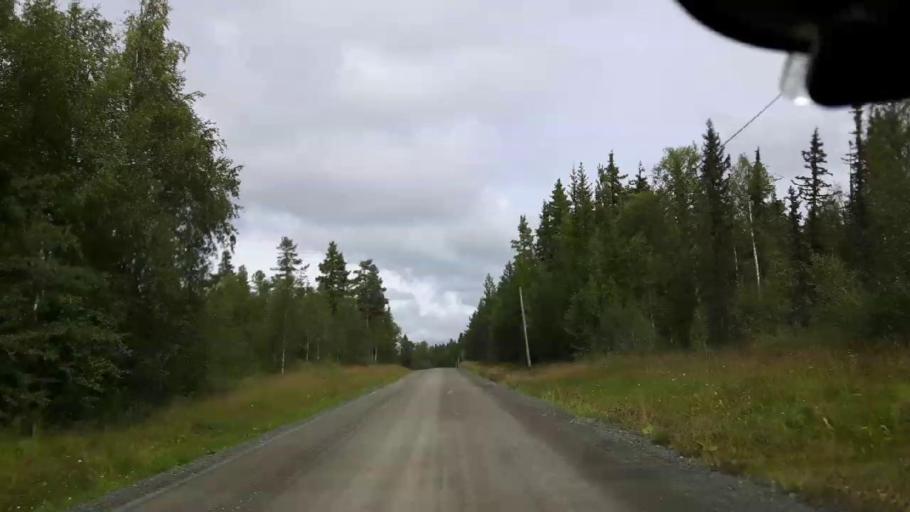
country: SE
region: Jaemtland
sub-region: Krokoms Kommun
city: Valla
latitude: 63.4033
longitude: 14.0939
